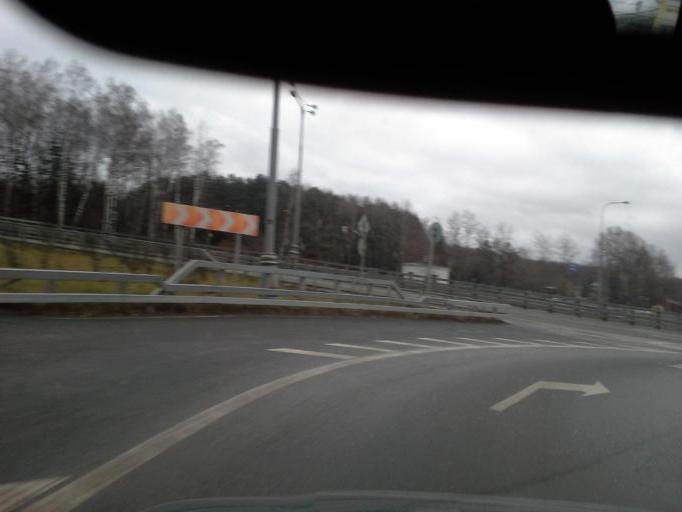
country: RU
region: Moskovskaya
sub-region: Leninskiy Rayon
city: Vnukovo
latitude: 55.6290
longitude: 37.3130
